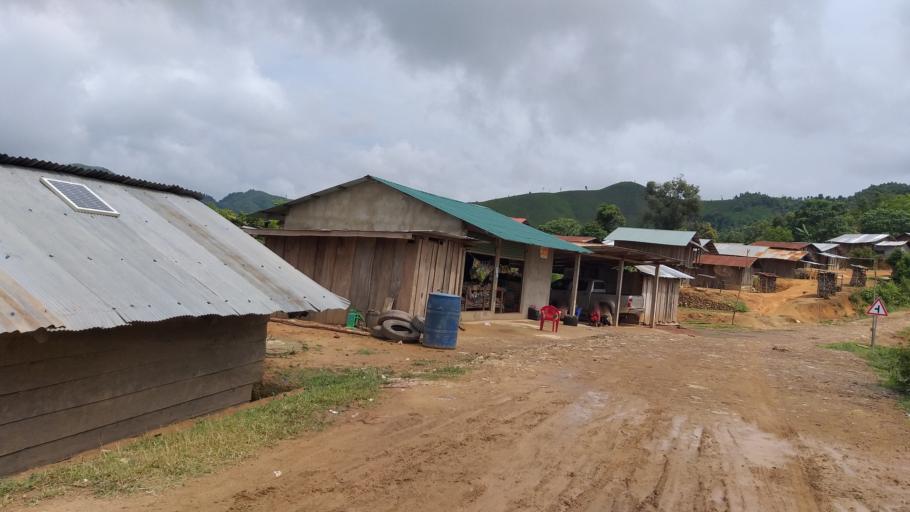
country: LA
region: Phongsali
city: Khoa
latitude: 21.3924
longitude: 102.6410
